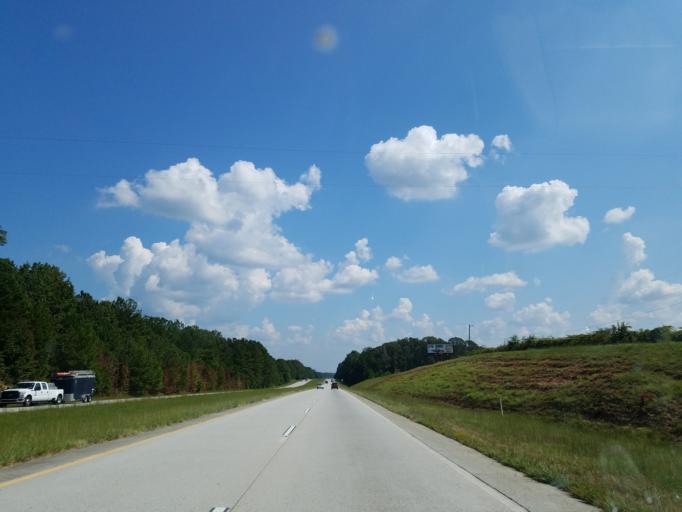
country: US
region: Georgia
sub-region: Oconee County
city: Bogart
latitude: 33.9399
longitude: -83.5539
